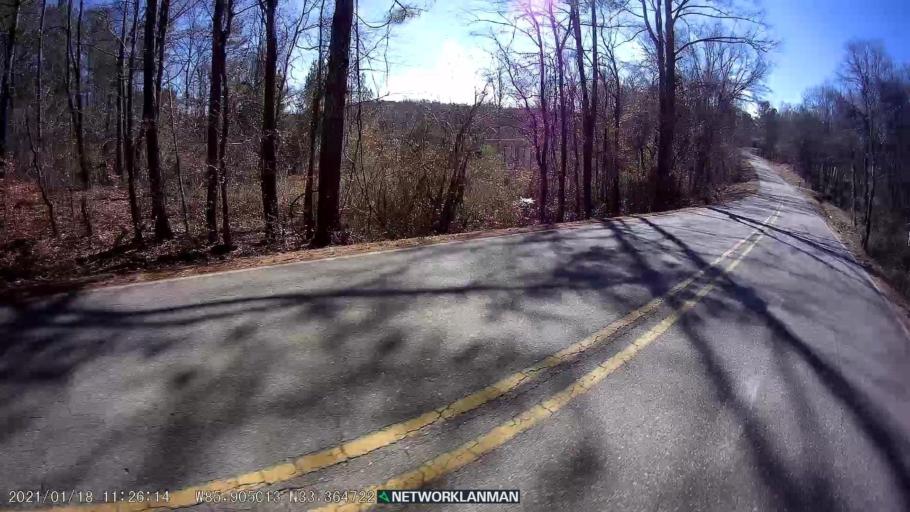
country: US
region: Alabama
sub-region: Clay County
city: Ashland
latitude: 33.3646
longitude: -85.9052
